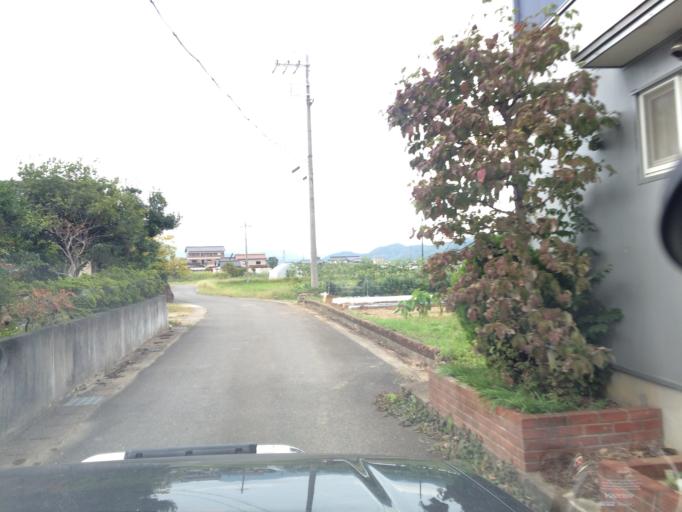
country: JP
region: Hyogo
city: Toyooka
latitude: 35.5144
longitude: 134.8287
